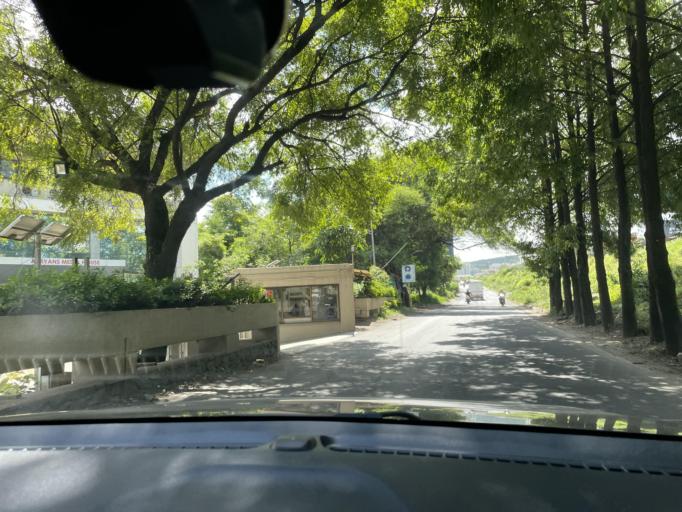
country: IN
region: Maharashtra
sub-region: Pune Division
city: Shivaji Nagar
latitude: 18.5270
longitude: 73.7763
